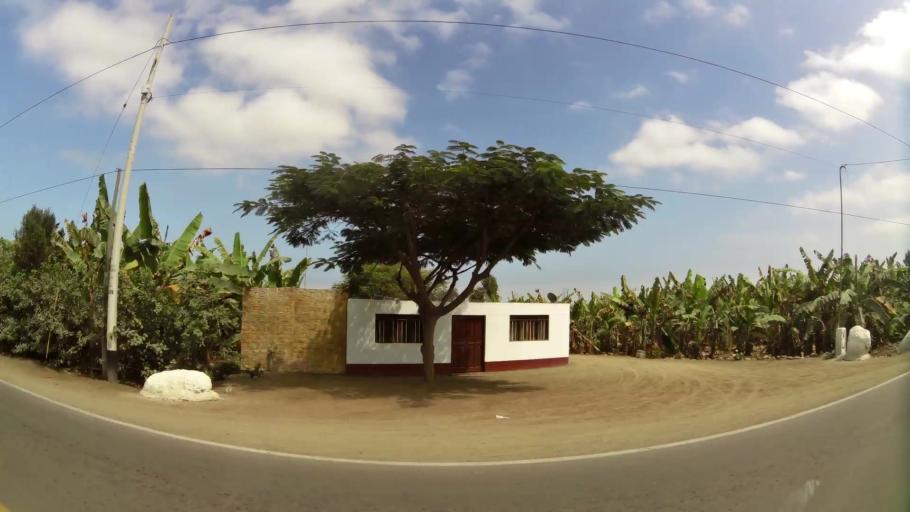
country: PE
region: Lima
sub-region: Provincia de Canete
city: Mala
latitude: -12.6833
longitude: -76.6273
